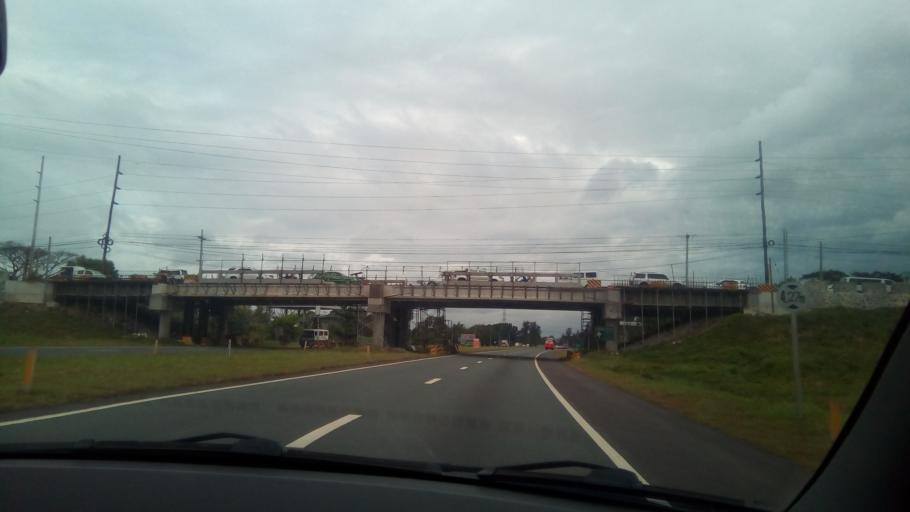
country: PH
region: Calabarzon
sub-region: Province of Batangas
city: Tanauan
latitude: 14.0868
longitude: 121.1330
